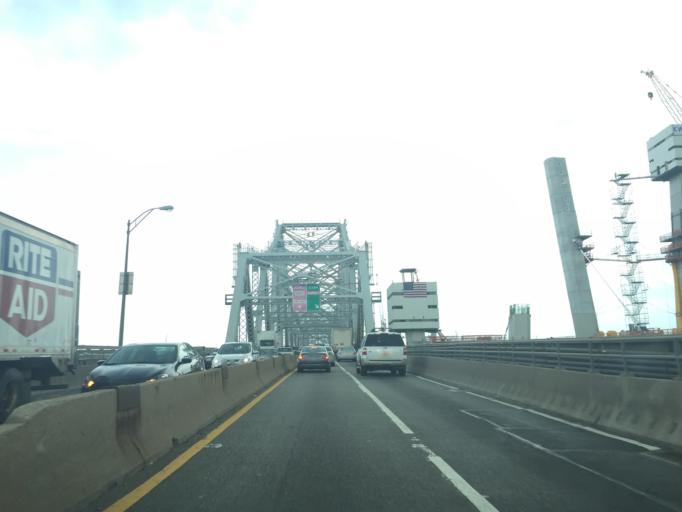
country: US
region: New Jersey
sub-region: Union County
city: Elizabeth
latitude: 40.6371
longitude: -74.1995
